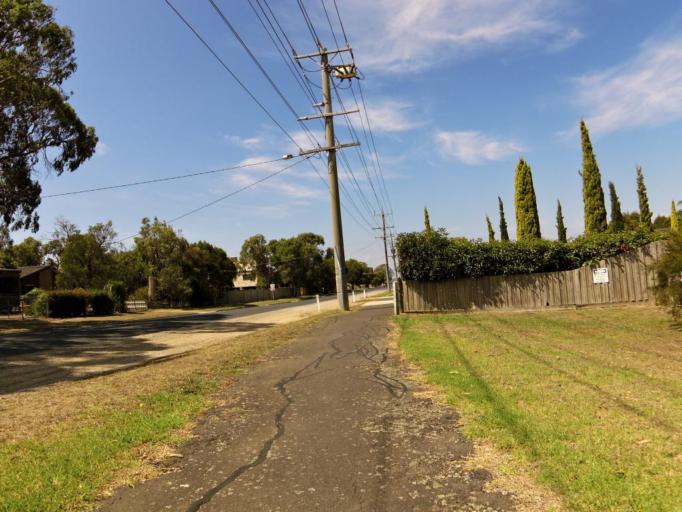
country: AU
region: Victoria
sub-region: Mornington Peninsula
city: Hastings
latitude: -38.3162
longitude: 145.1876
